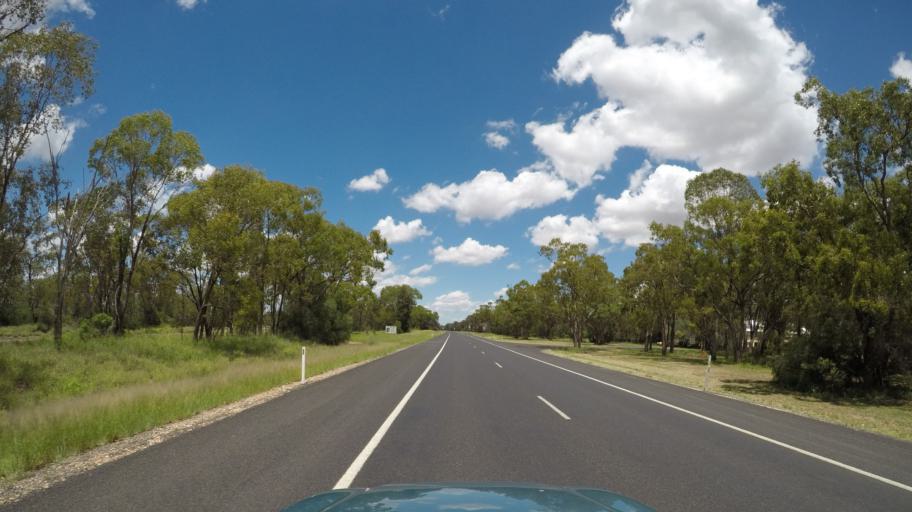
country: AU
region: Queensland
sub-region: Goondiwindi
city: Goondiwindi
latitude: -28.0797
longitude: 150.7407
